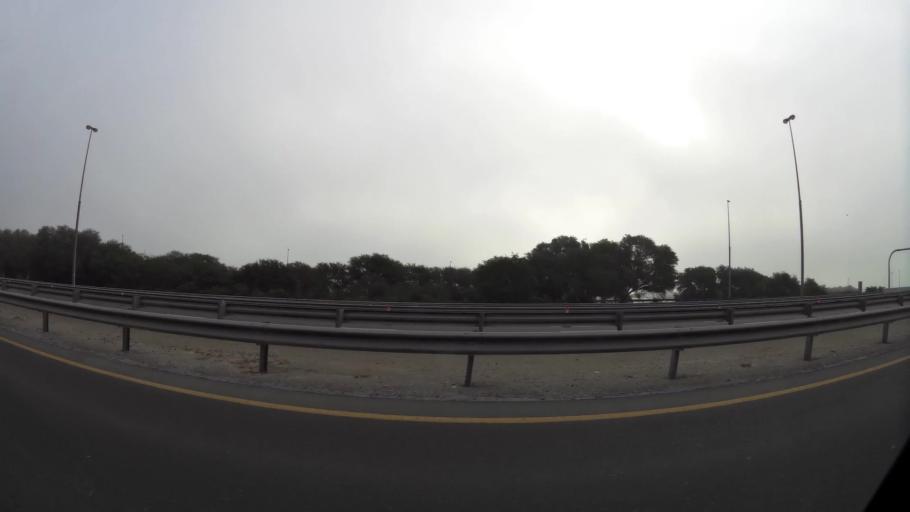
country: AE
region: Dubai
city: Dubai
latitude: 25.1812
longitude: 55.3143
